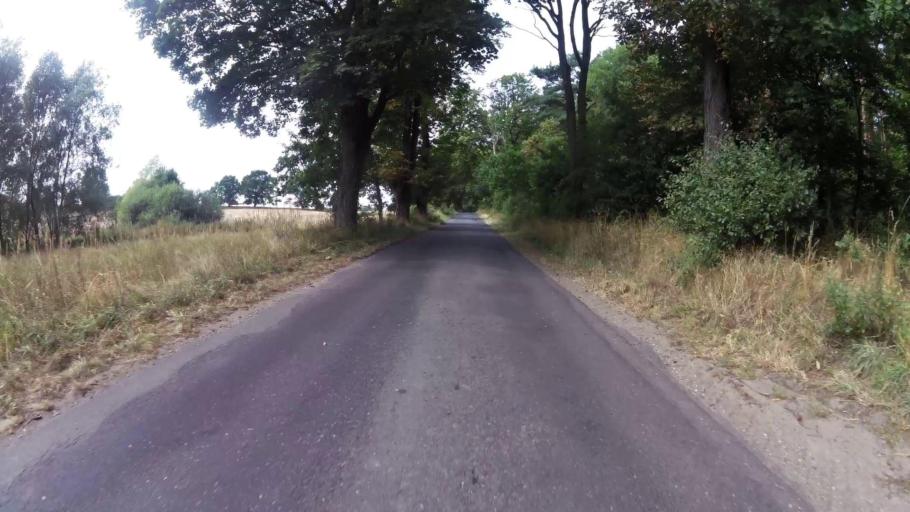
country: PL
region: West Pomeranian Voivodeship
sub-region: Powiat gryfinski
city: Mieszkowice
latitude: 52.8734
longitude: 14.5058
